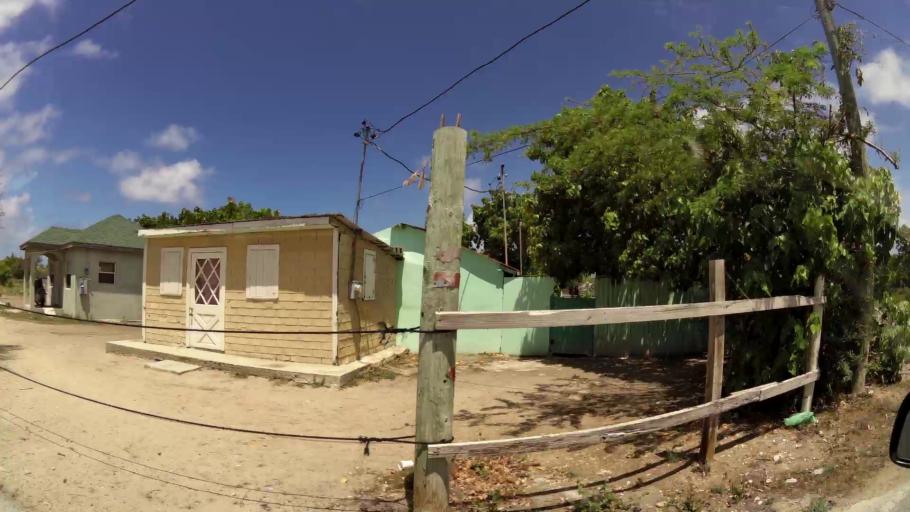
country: TC
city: Cockburn Town
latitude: 21.4587
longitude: -71.1439
